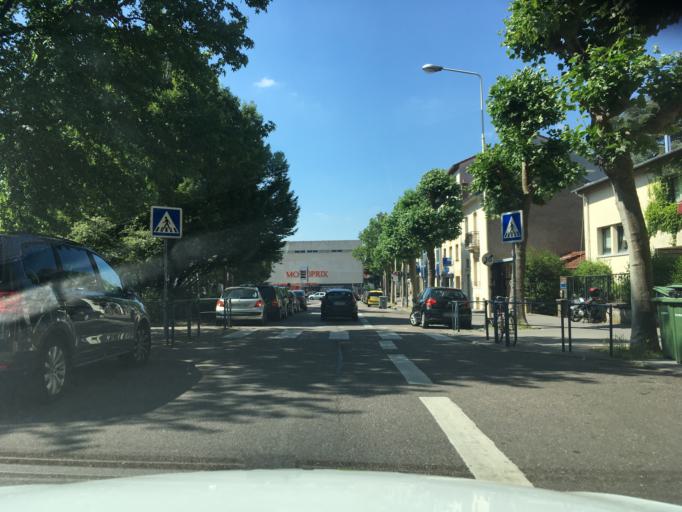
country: FR
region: Lorraine
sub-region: Departement de Meurthe-et-Moselle
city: Villers-les-Nancy
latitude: 48.6741
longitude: 6.1639
